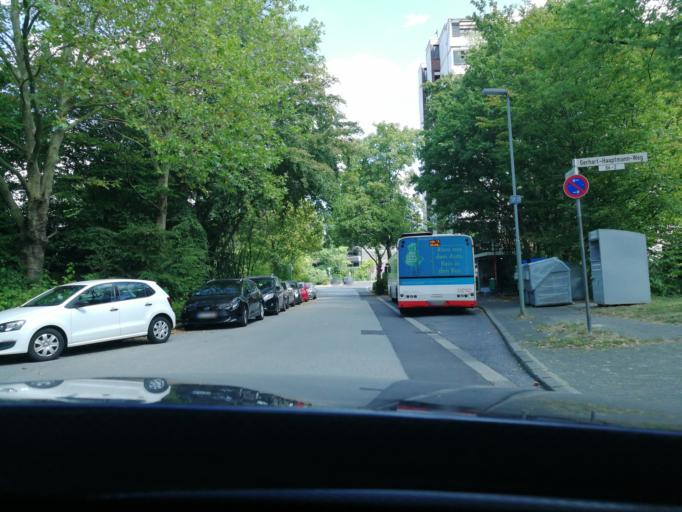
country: DE
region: North Rhine-Westphalia
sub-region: Regierungsbezirk Dusseldorf
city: Neuss
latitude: 51.1493
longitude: 6.7366
